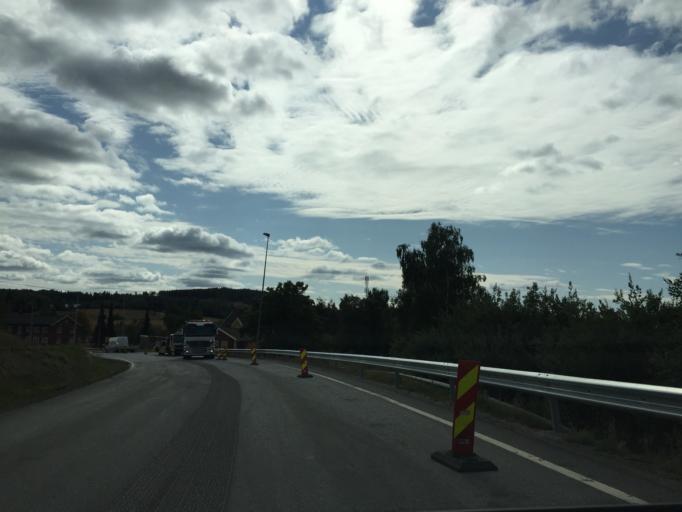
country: NO
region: Ostfold
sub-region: Hobol
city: Elvestad
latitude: 59.6240
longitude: 10.9473
